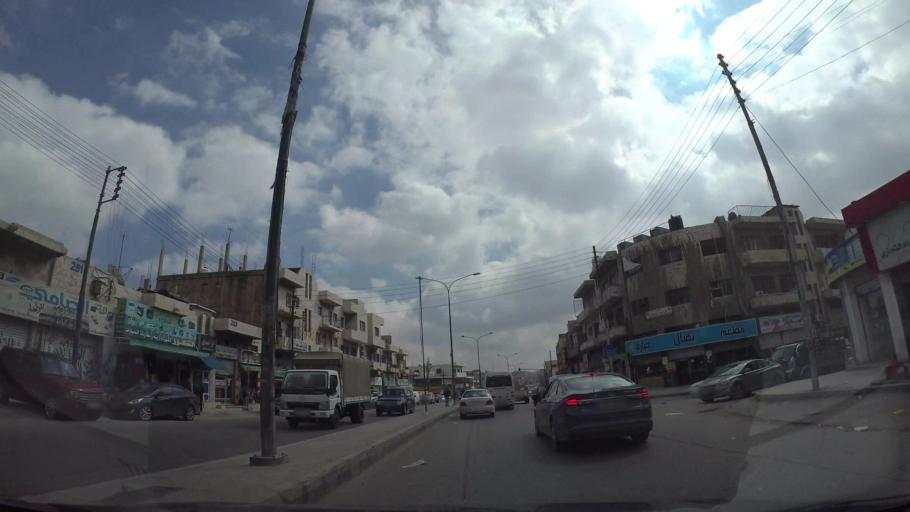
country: JO
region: Amman
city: Al Quwaysimah
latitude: 31.9276
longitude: 35.9377
